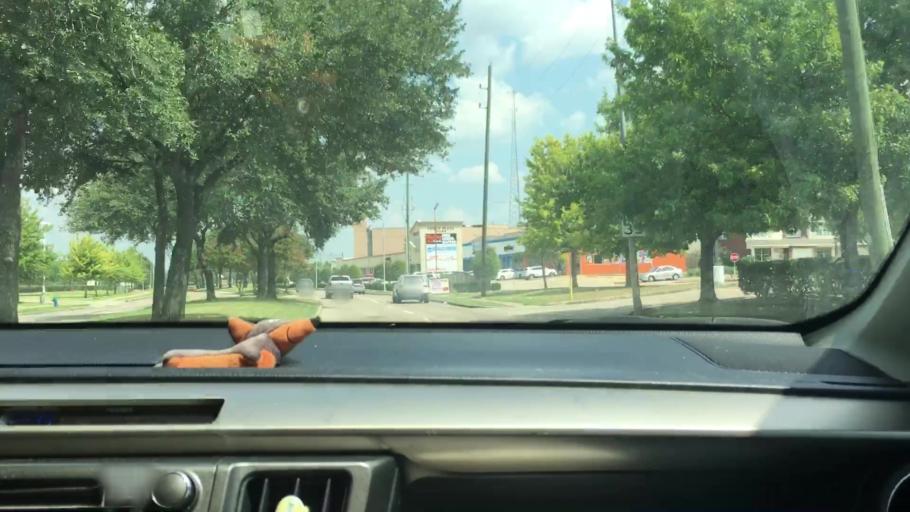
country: US
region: Texas
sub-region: Fort Bend County
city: Mission Bend
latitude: 29.7242
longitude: -95.6049
